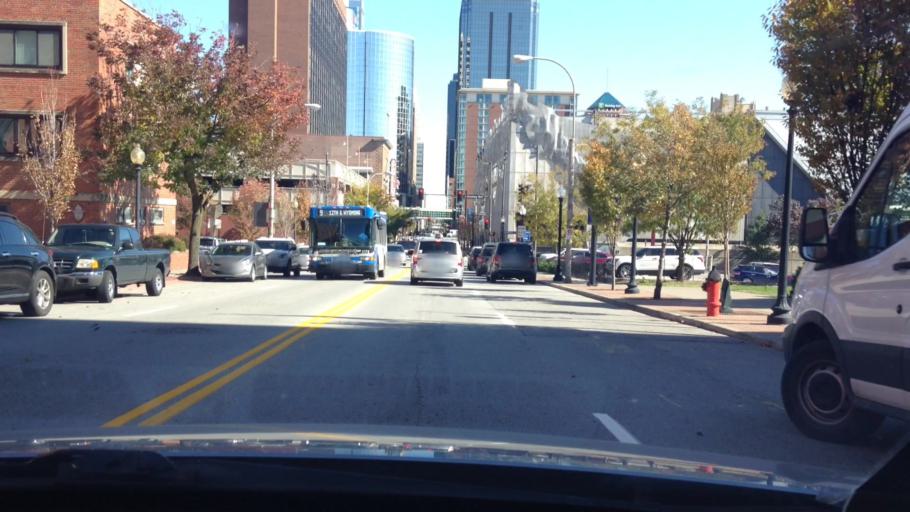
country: US
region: Missouri
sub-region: Jackson County
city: Kansas City
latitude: 39.1001
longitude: -94.5896
